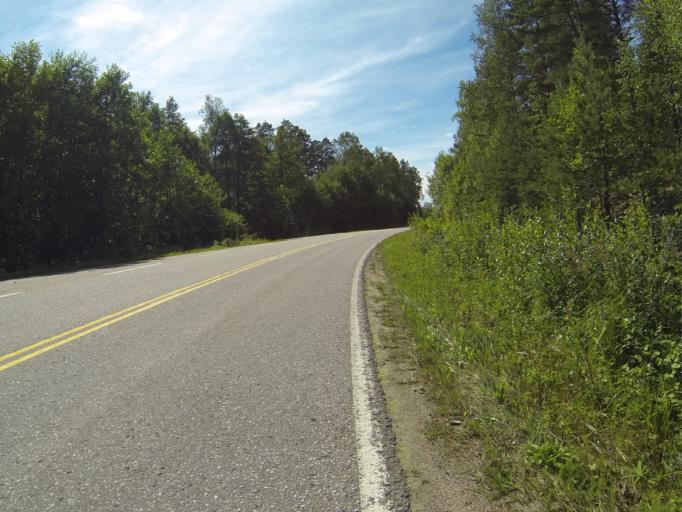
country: FI
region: Varsinais-Suomi
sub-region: Salo
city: Saerkisalo
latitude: 60.2642
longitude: 22.9736
